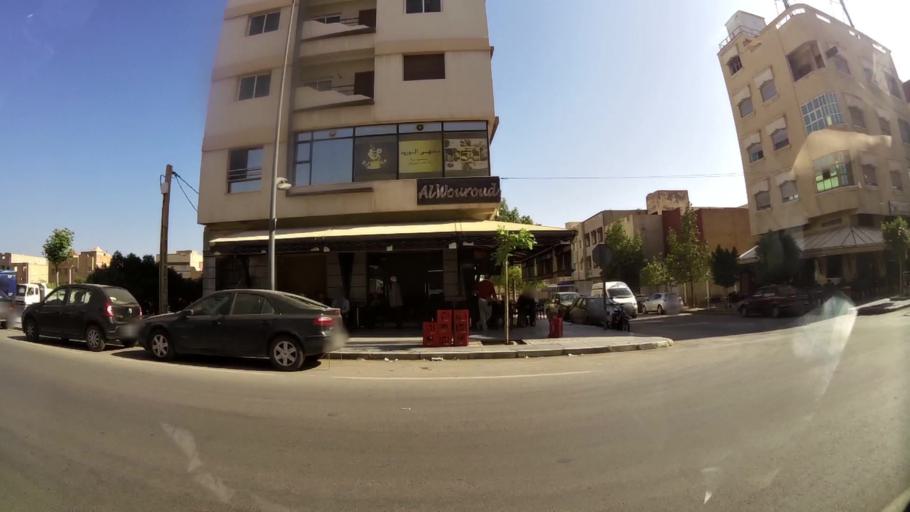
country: MA
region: Oriental
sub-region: Oujda-Angad
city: Oujda
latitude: 34.6816
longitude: -1.9392
